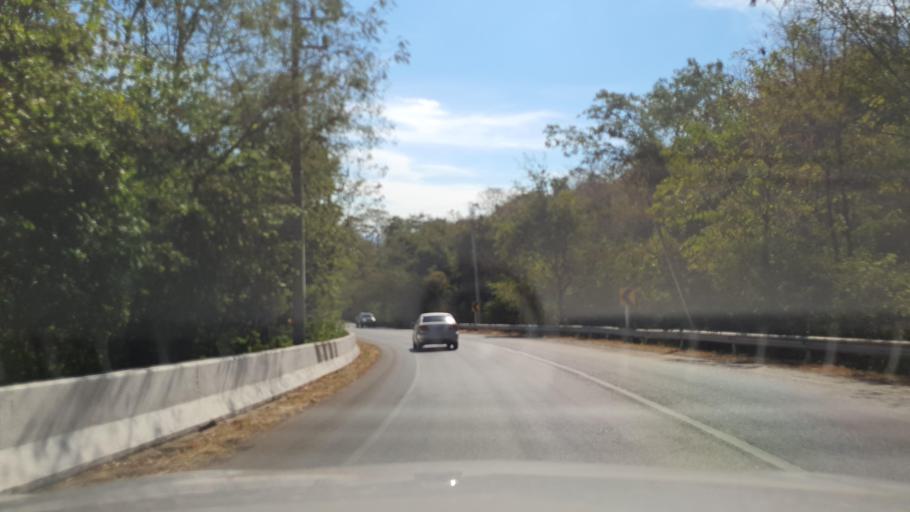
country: TH
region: Kalasin
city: Khao Wong
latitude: 16.7596
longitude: 104.1286
